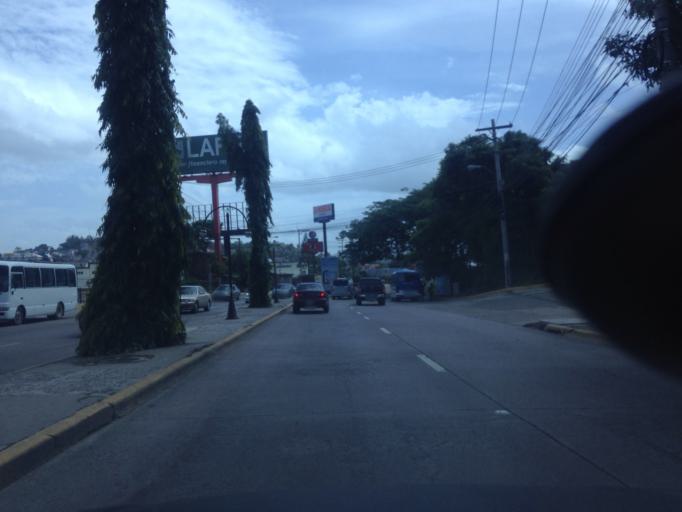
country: HN
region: Francisco Morazan
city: Tegucigalpa
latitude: 14.0636
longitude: -87.2191
